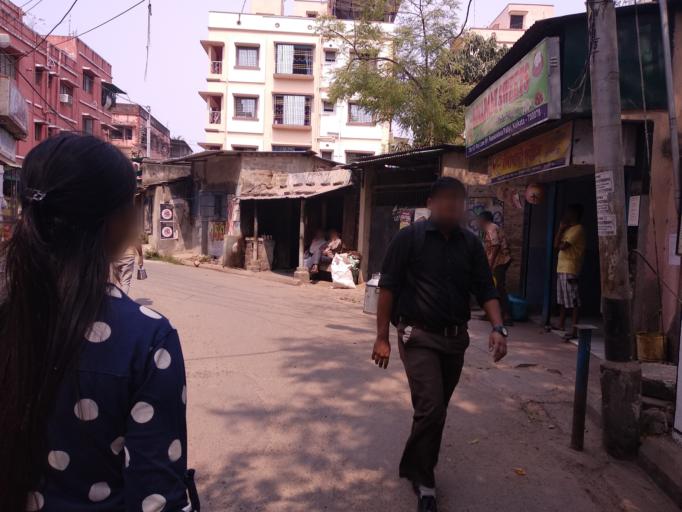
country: IN
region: West Bengal
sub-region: Kolkata
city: Kolkata
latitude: 22.5037
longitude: 88.3787
